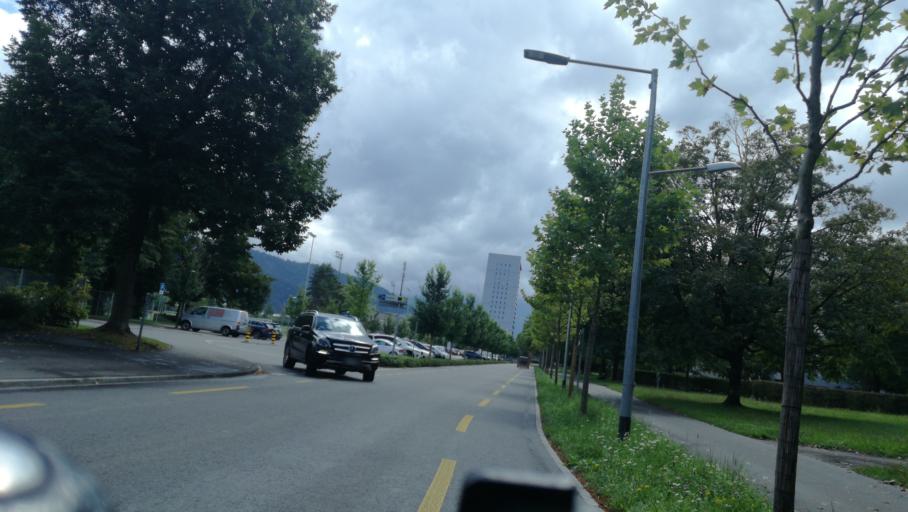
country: CH
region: Zug
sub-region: Zug
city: Zug
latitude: 47.1805
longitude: 8.5079
